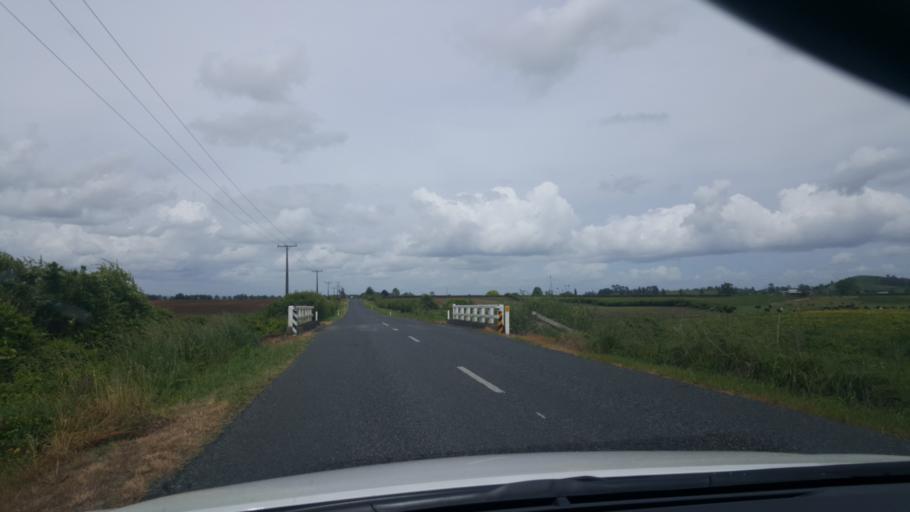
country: NZ
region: Waikato
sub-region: Matamata-Piako District
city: Matamata
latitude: -37.8755
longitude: 175.7264
